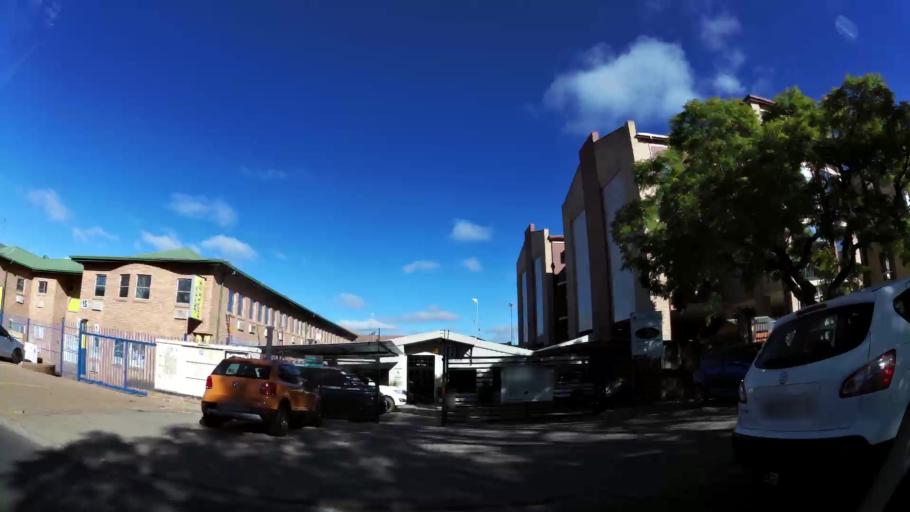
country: ZA
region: Limpopo
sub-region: Capricorn District Municipality
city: Polokwane
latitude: -23.9165
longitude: 29.4580
